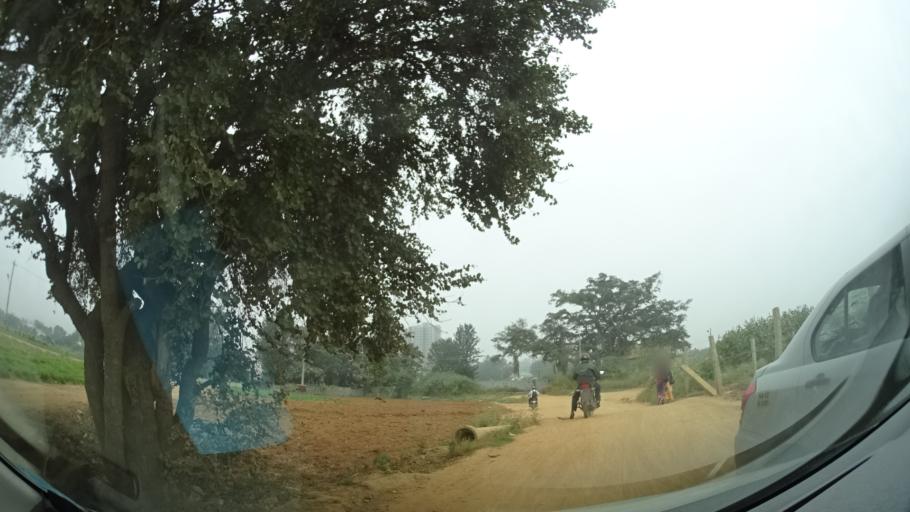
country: IN
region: Karnataka
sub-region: Bangalore Rural
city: Hoskote
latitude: 12.9638
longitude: 77.7312
